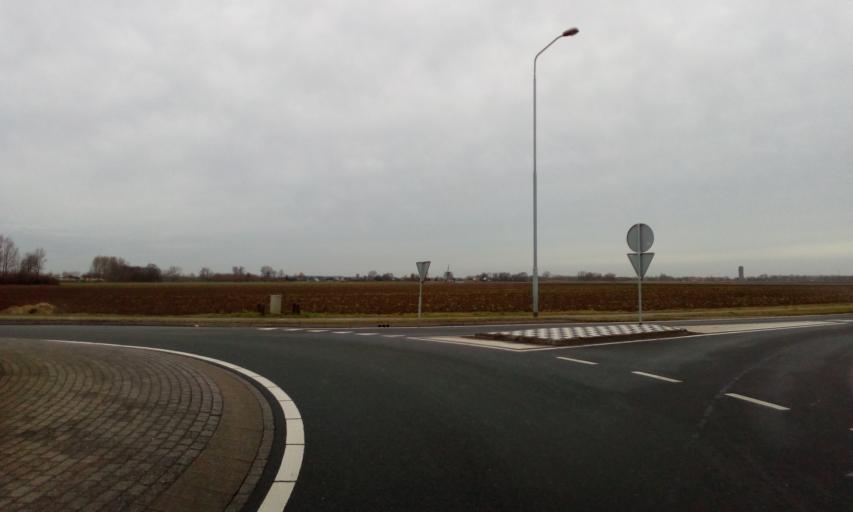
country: NL
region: North Brabant
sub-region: Gemeente Woudrichem
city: Almkerk
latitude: 51.7753
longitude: 4.9633
